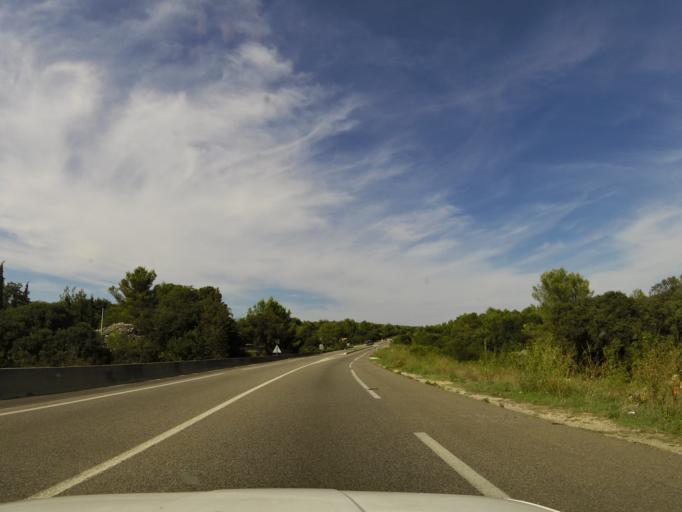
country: FR
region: Languedoc-Roussillon
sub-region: Departement du Gard
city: Nimes
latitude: 43.8463
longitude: 4.3172
